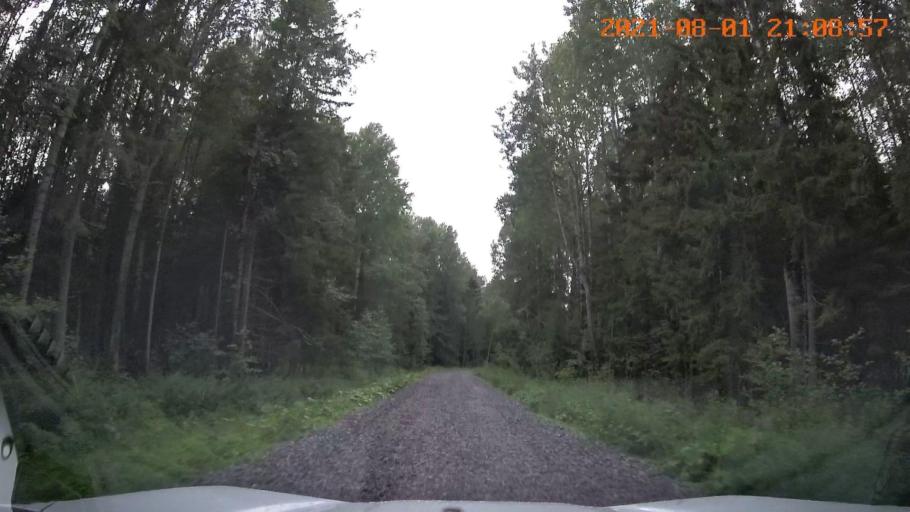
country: RU
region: Leningrad
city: Syas'stroy
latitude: 60.5099
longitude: 32.6496
